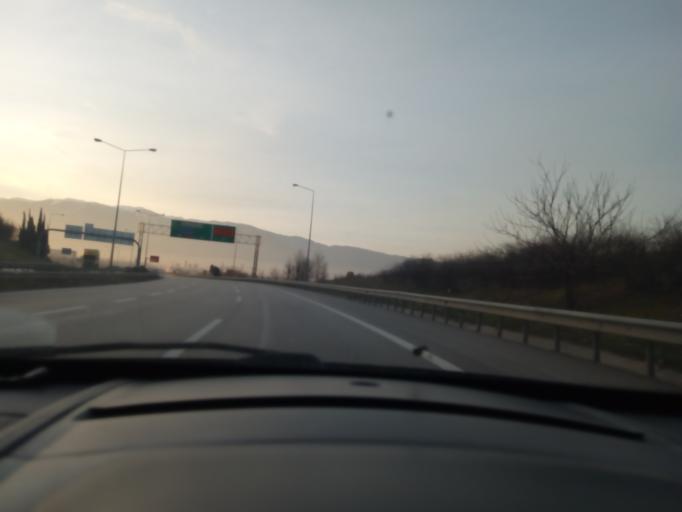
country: TR
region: Bursa
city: Demirtas
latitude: 40.2824
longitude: 29.0408
